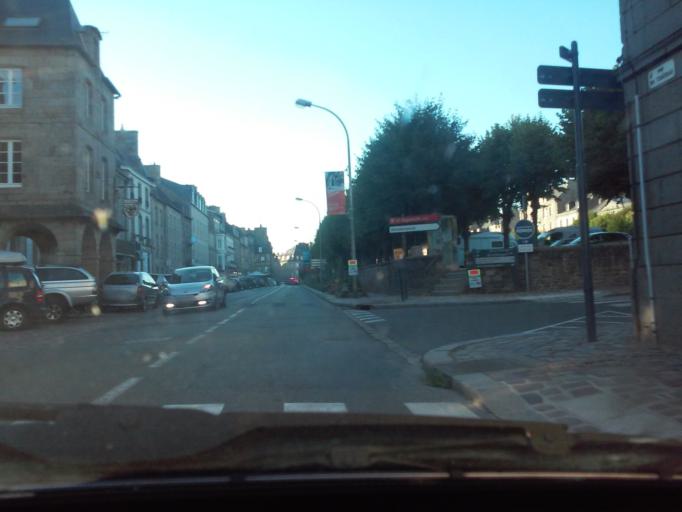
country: FR
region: Brittany
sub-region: Departement des Cotes-d'Armor
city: Lehon
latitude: 48.4508
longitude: -2.0441
